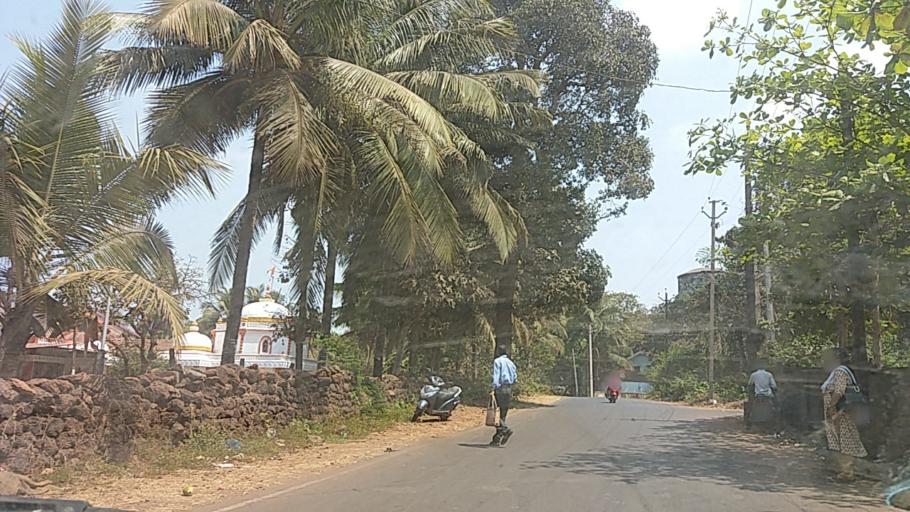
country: IN
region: Goa
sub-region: North Goa
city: Panaji
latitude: 15.5163
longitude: 73.8362
